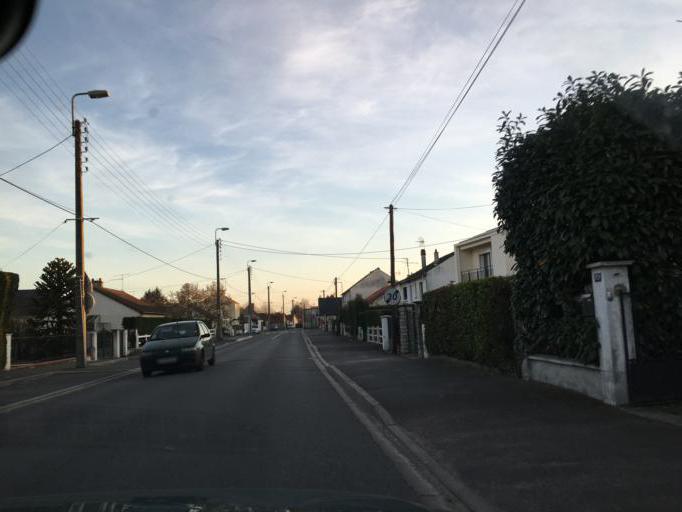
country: FR
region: Centre
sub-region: Departement du Loiret
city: Saran
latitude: 47.9437
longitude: 1.8711
